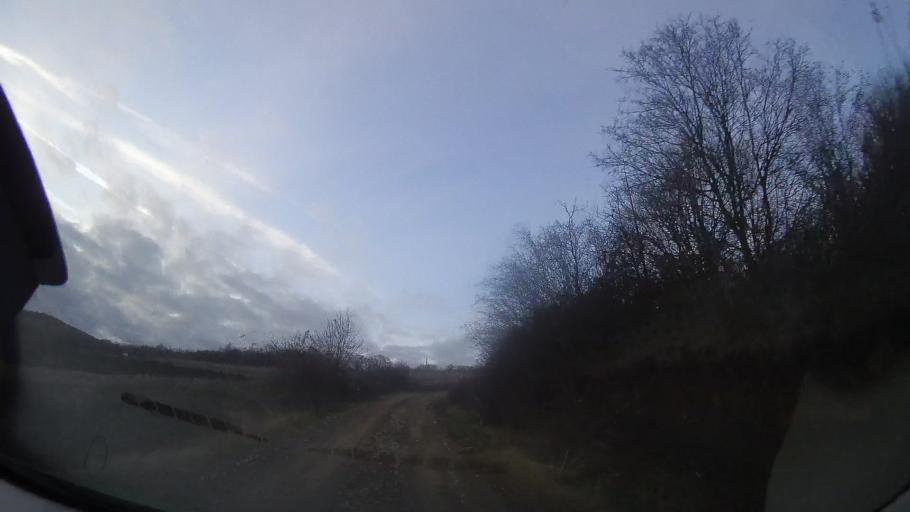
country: RO
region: Cluj
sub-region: Comuna Palatca
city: Palatca
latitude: 46.8590
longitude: 24.0274
